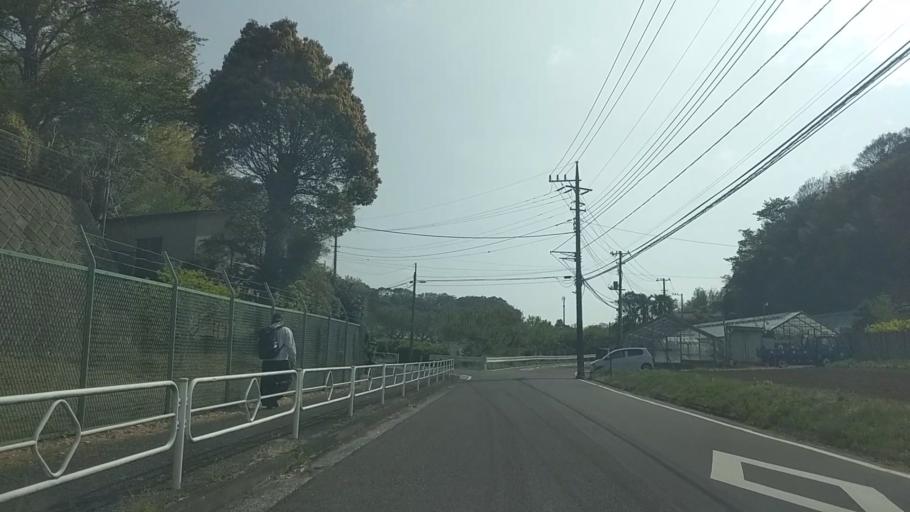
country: JP
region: Kanagawa
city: Kamakura
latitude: 35.3860
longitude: 139.5635
